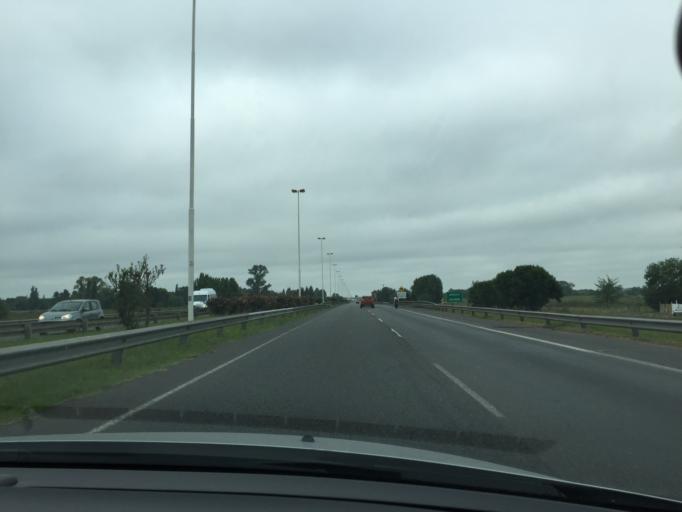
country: AR
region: Buenos Aires
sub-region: Partido de Ezeiza
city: Ezeiza
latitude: -34.8675
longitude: -58.5765
